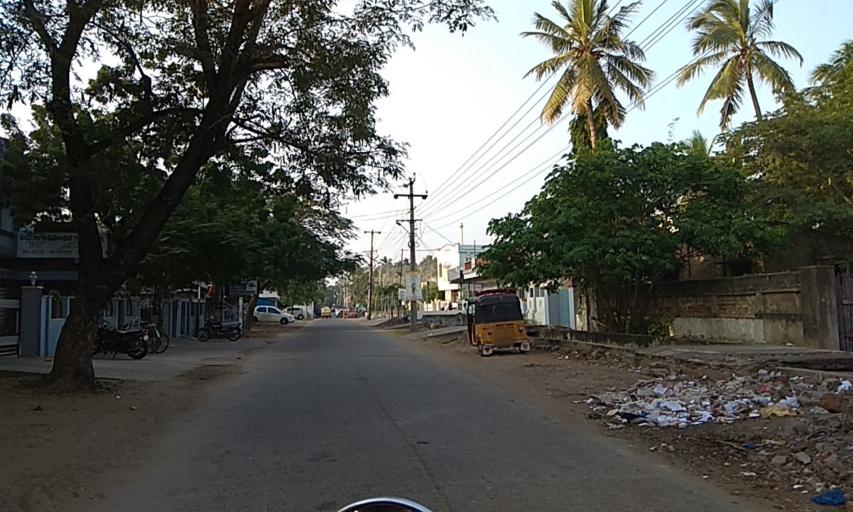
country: IN
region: Andhra Pradesh
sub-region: Krishna
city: Machilipatnam
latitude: 16.1868
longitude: 81.1349
